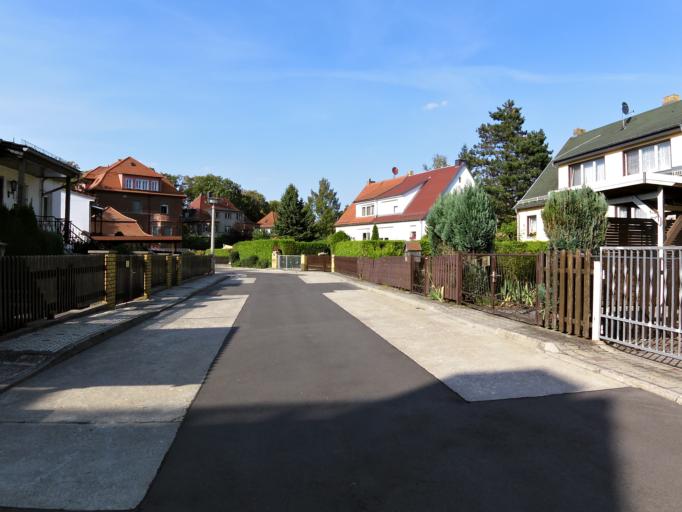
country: DE
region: Saxony
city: Leipzig
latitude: 51.3523
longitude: 12.3211
